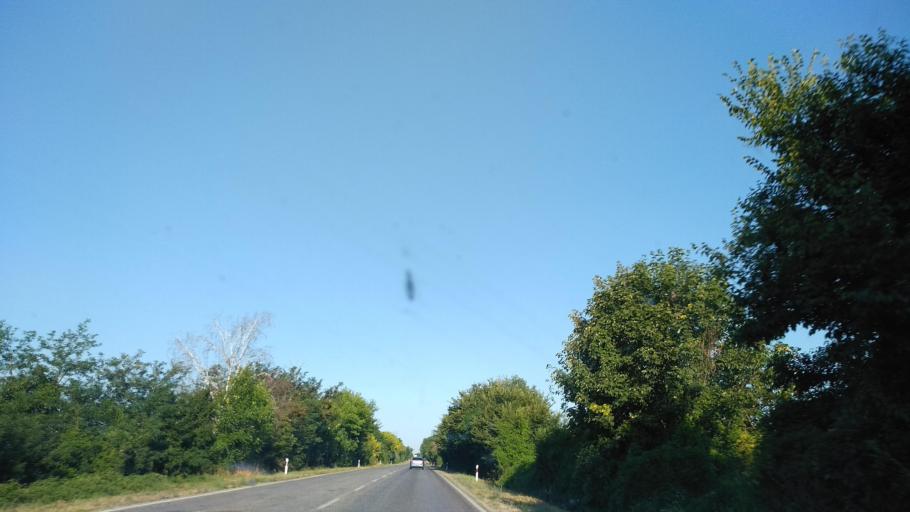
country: BG
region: Gabrovo
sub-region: Obshtina Dryanovo
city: Dryanovo
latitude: 43.0874
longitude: 25.4488
